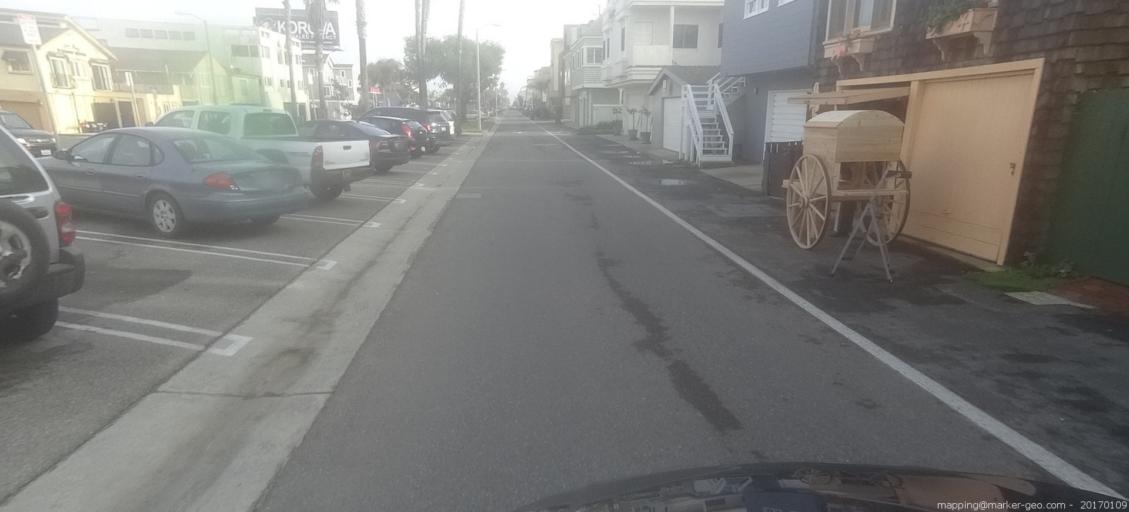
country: US
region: California
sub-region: Orange County
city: Seal Beach
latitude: 33.7215
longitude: -118.0758
